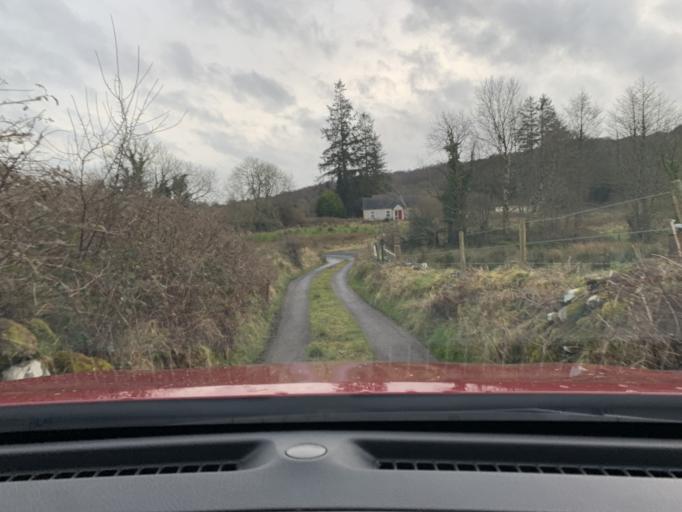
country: IE
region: Connaught
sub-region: Sligo
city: Ballymote
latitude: 53.9705
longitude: -8.4726
